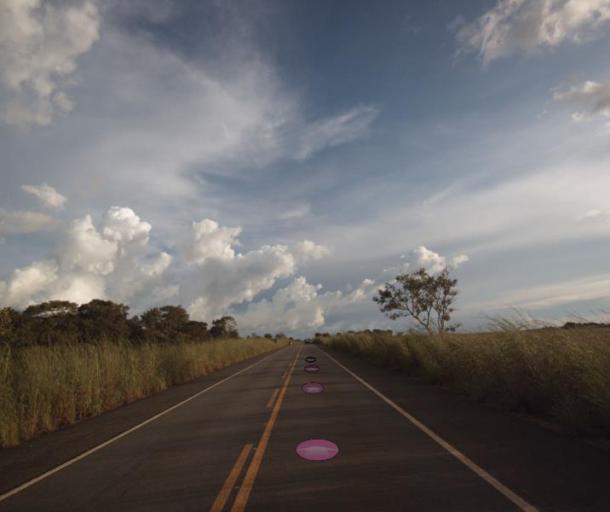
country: BR
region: Goias
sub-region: Niquelandia
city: Niquelandia
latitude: -14.7386
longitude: -48.6160
